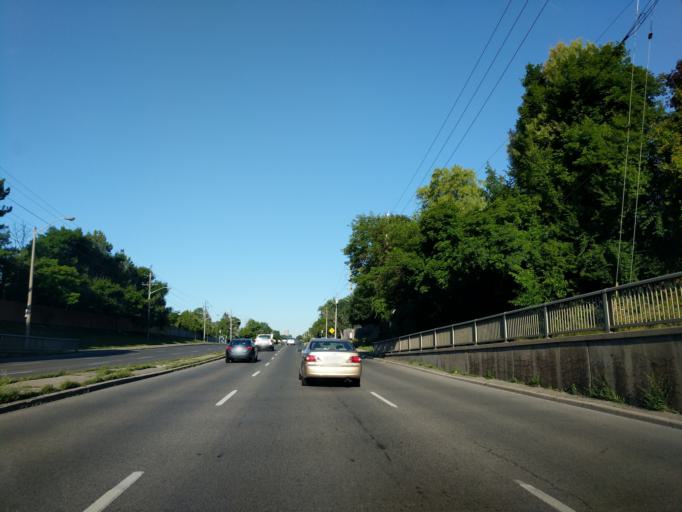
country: CA
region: Ontario
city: Willowdale
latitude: 43.8067
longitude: -79.3812
